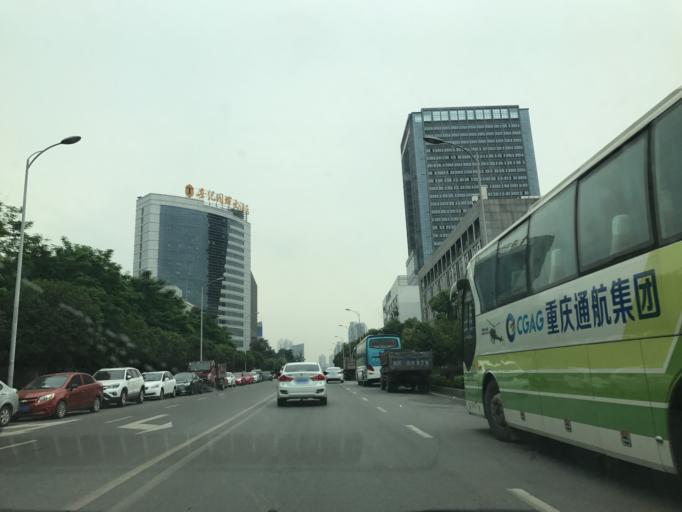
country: CN
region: Chongqing Shi
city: Cuntan
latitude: 29.6097
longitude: 106.5534
